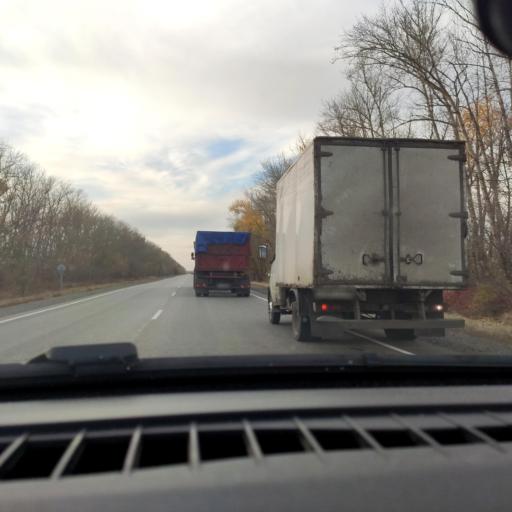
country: RU
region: Voronezj
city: Ostrogozhsk
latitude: 50.9598
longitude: 39.0266
